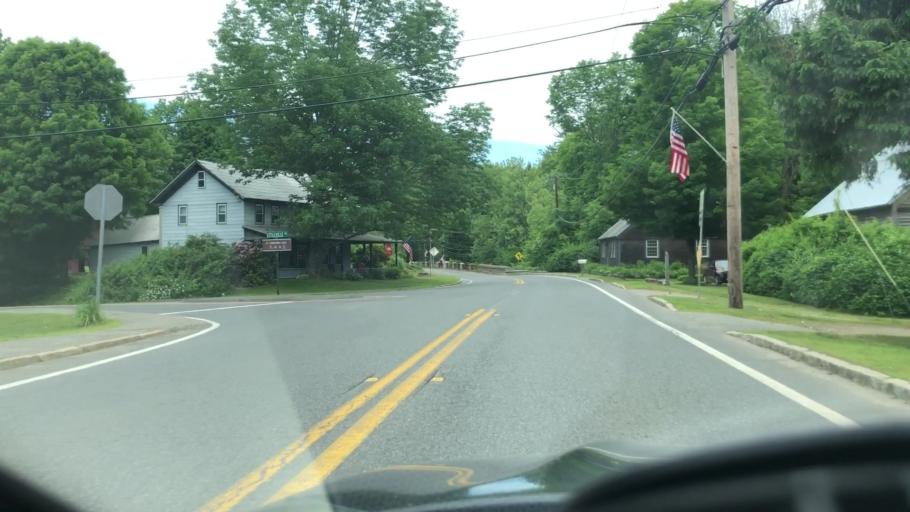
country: US
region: Massachusetts
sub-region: Hampshire County
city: Westhampton
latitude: 42.2485
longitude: -72.8683
